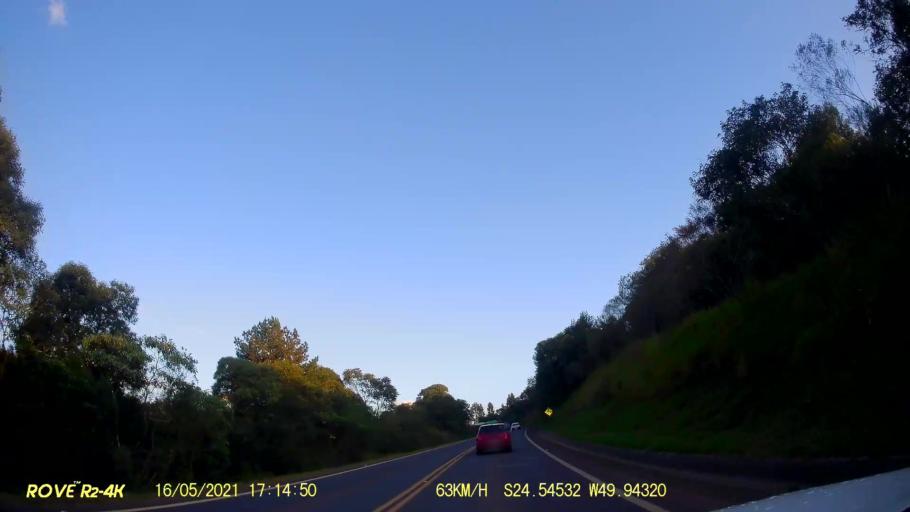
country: BR
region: Parana
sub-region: Pirai Do Sul
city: Pirai do Sul
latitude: -24.5455
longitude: -49.9431
